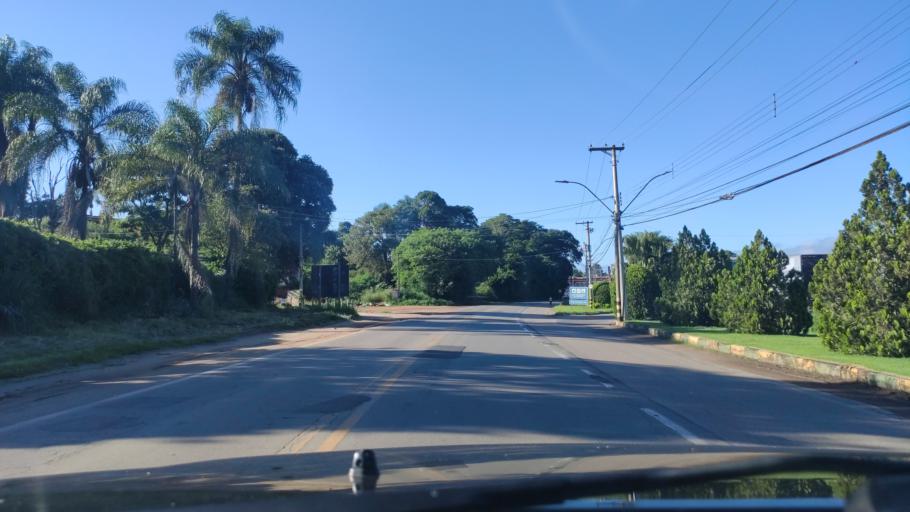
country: BR
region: Sao Paulo
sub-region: Socorro
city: Socorro
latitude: -22.6160
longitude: -46.5315
